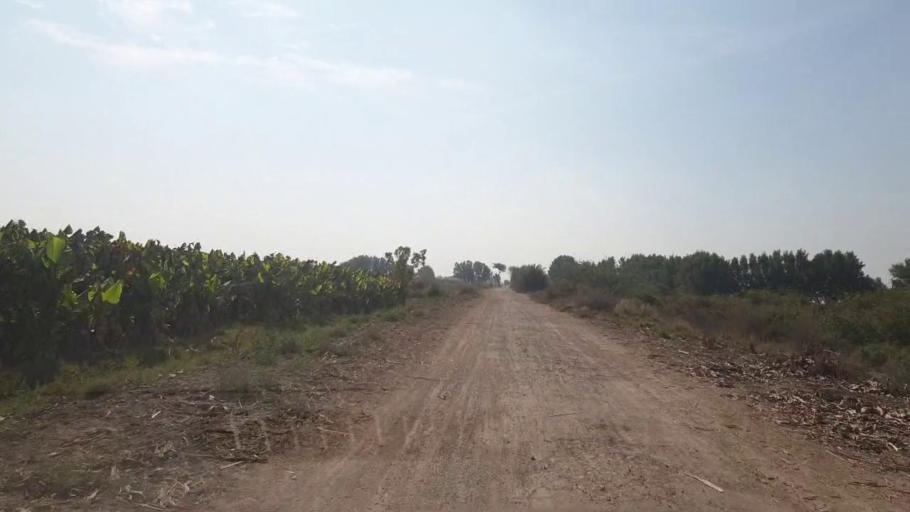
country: PK
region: Sindh
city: Mirwah Gorchani
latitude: 25.3747
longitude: 69.2026
